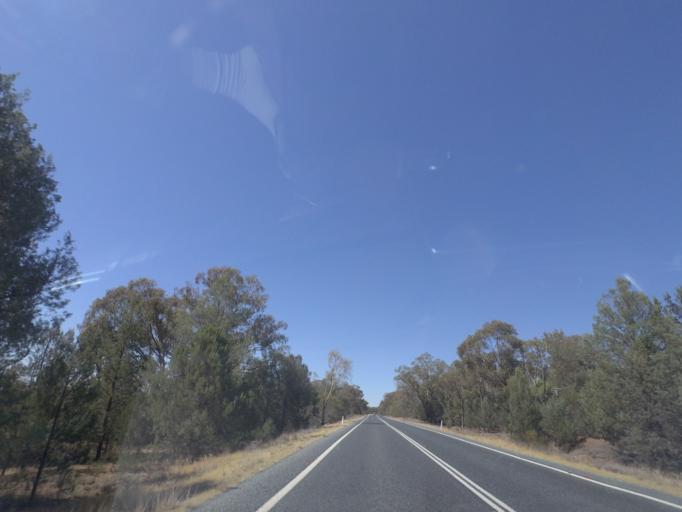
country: AU
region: New South Wales
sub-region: Narrandera
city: Narrandera
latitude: -34.4339
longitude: 146.8426
